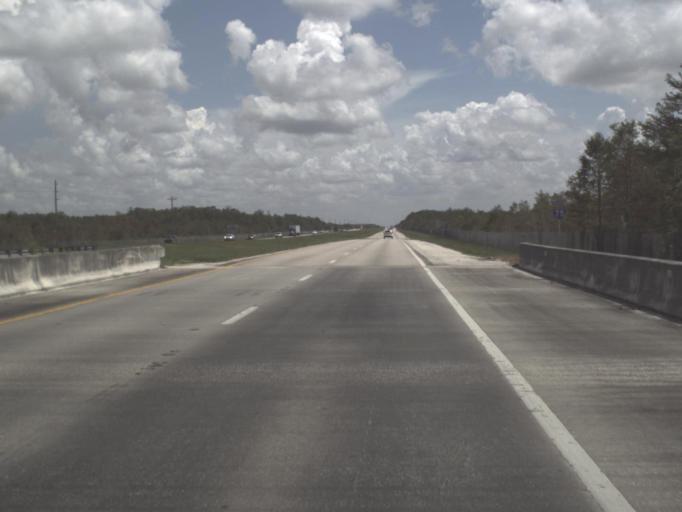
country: US
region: Florida
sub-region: Collier County
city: Immokalee
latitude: 26.1685
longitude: -81.0629
